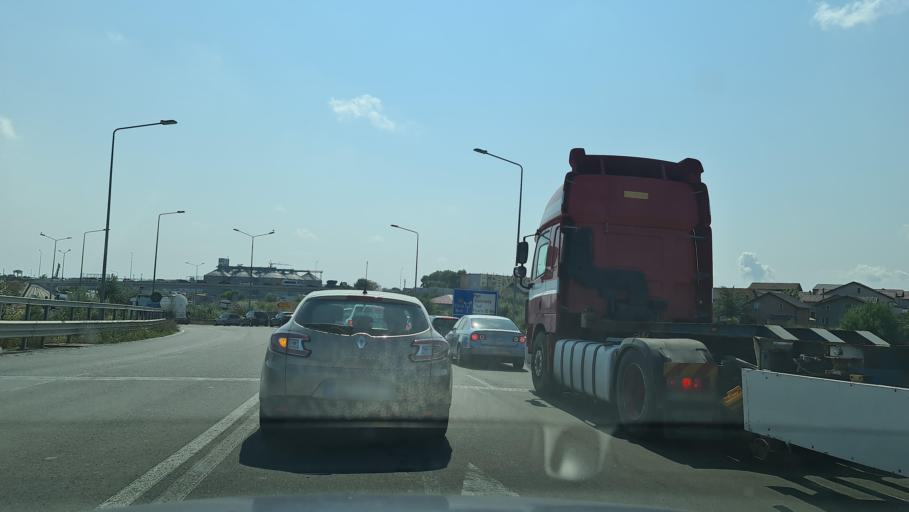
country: RO
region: Constanta
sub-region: Comuna Agigea
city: Agigea
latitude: 44.0964
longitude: 28.6365
